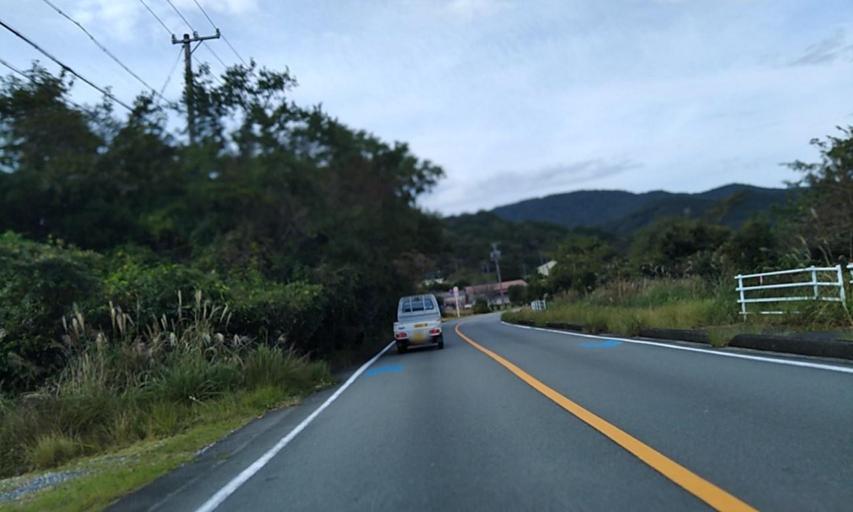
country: JP
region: Mie
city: Ise
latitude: 34.3058
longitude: 136.6360
